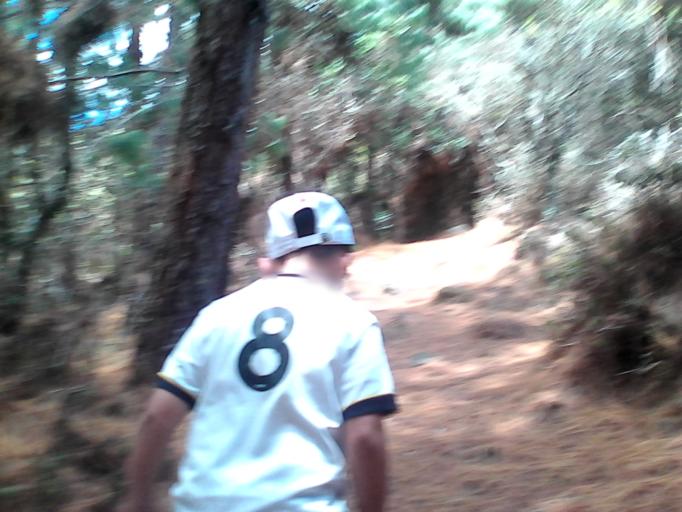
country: CO
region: Boyaca
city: Santa Rosa de Viterbo
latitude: 5.9081
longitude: -73.0557
